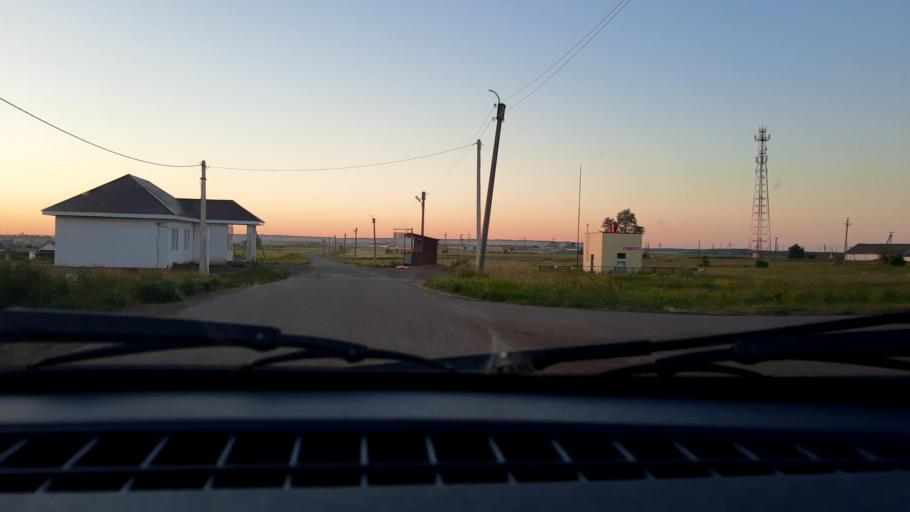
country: RU
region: Bashkortostan
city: Asanovo
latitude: 54.8905
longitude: 55.6243
